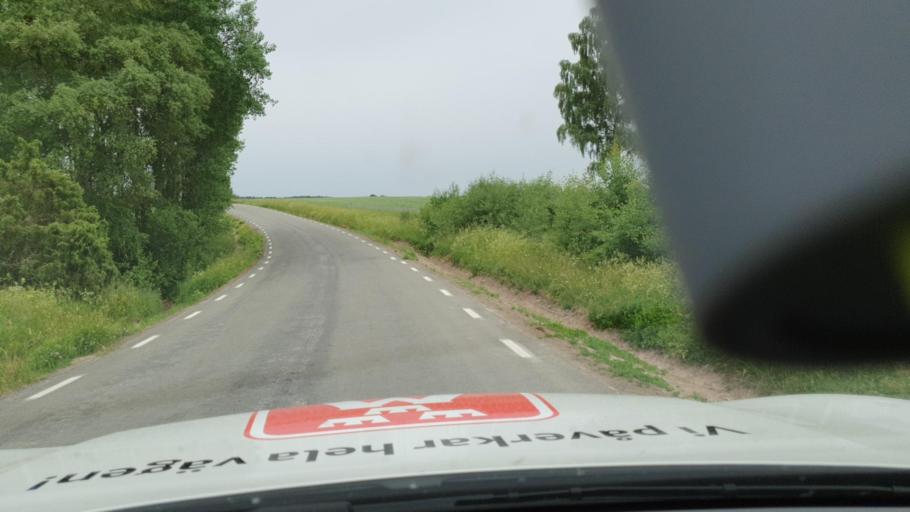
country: SE
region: Vaestra Goetaland
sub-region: Tidaholms Kommun
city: Olofstorp
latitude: 58.3053
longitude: 14.0638
